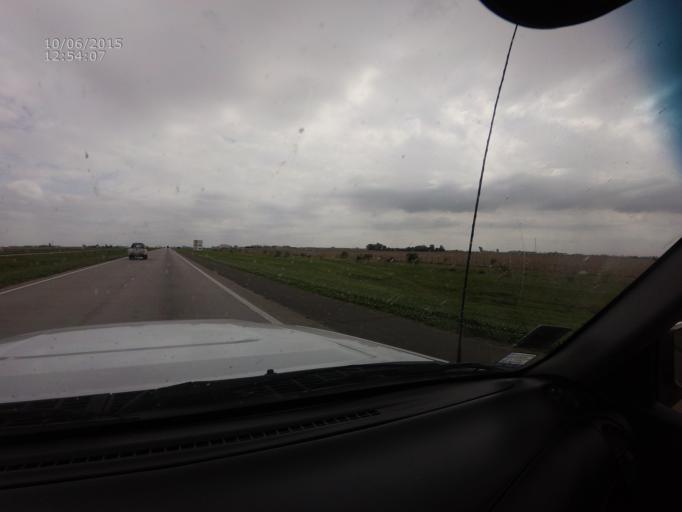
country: AR
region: Santa Fe
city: Armstrong
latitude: -32.8165
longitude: -61.5655
